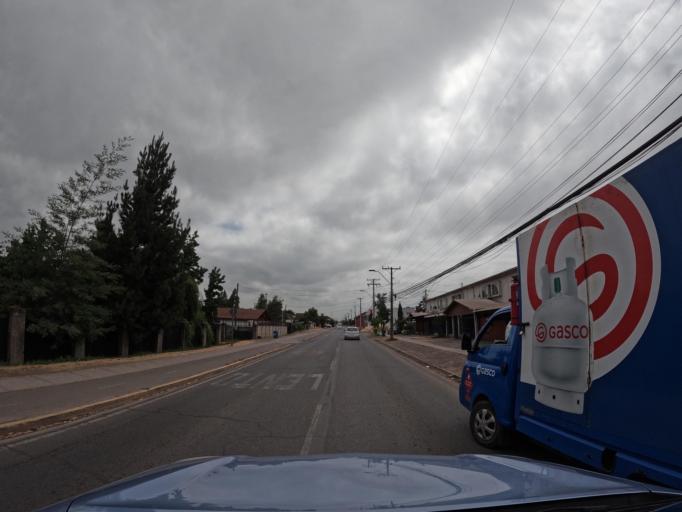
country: CL
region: O'Higgins
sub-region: Provincia de Colchagua
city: Chimbarongo
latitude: -34.7157
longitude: -71.0487
